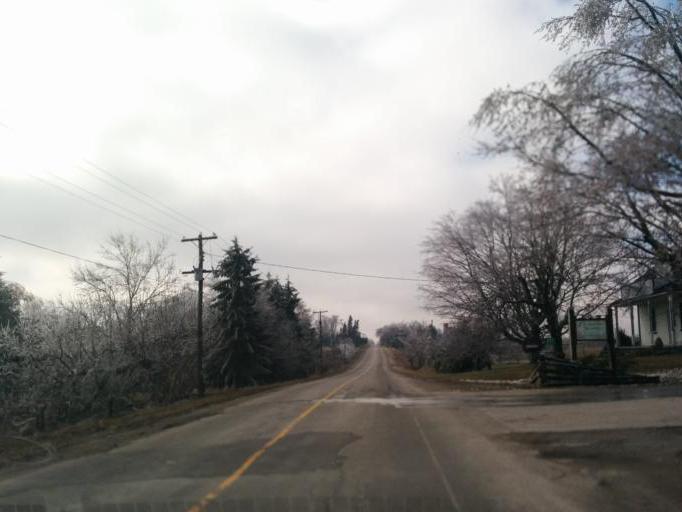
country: CA
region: Ontario
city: Waterloo
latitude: 43.6340
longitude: -80.5618
